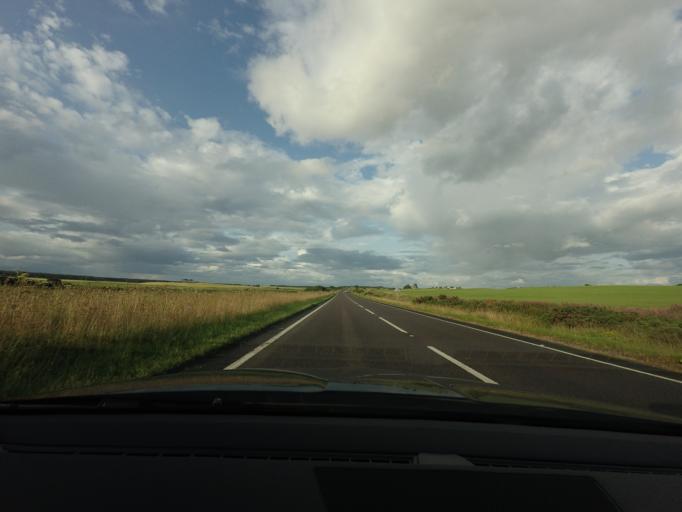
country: GB
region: Scotland
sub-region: Highland
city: Nairn
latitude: 57.5526
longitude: -3.9828
